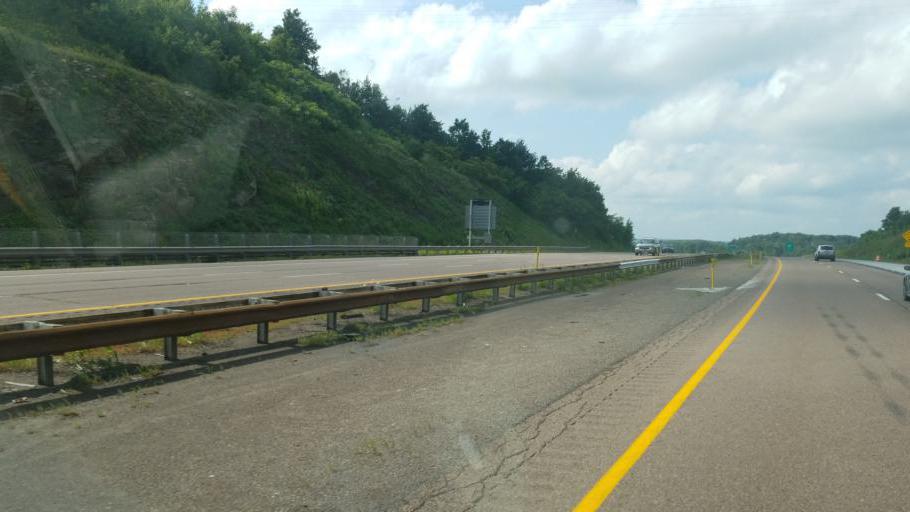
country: US
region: Maryland
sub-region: Allegany County
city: Frostburg
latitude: 39.6738
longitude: -78.9628
